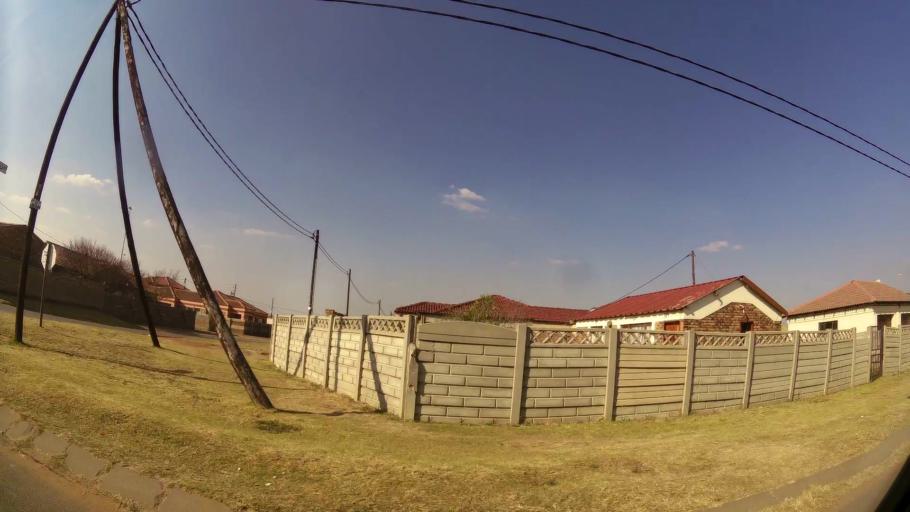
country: ZA
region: Gauteng
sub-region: Ekurhuleni Metropolitan Municipality
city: Benoni
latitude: -26.2242
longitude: 28.3225
